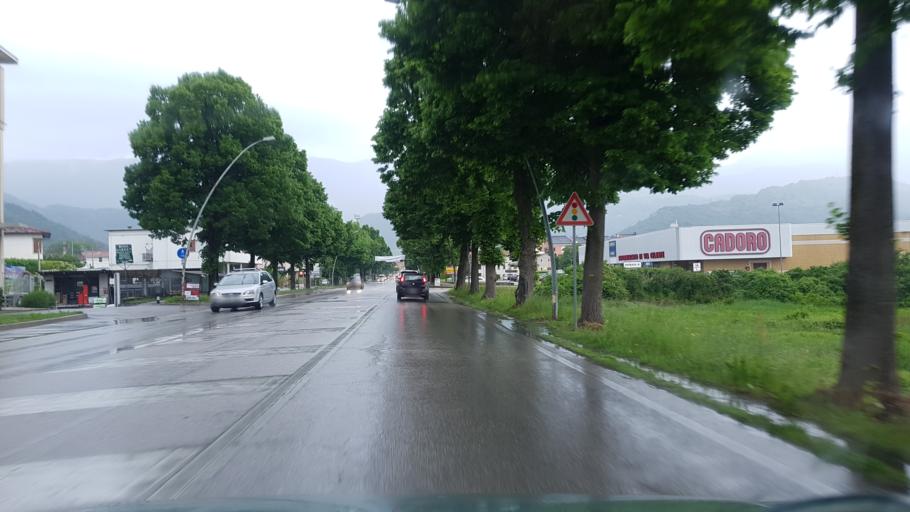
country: IT
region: Veneto
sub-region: Provincia di Treviso
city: Vittorio Veneto
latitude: 45.9745
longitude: 12.3082
